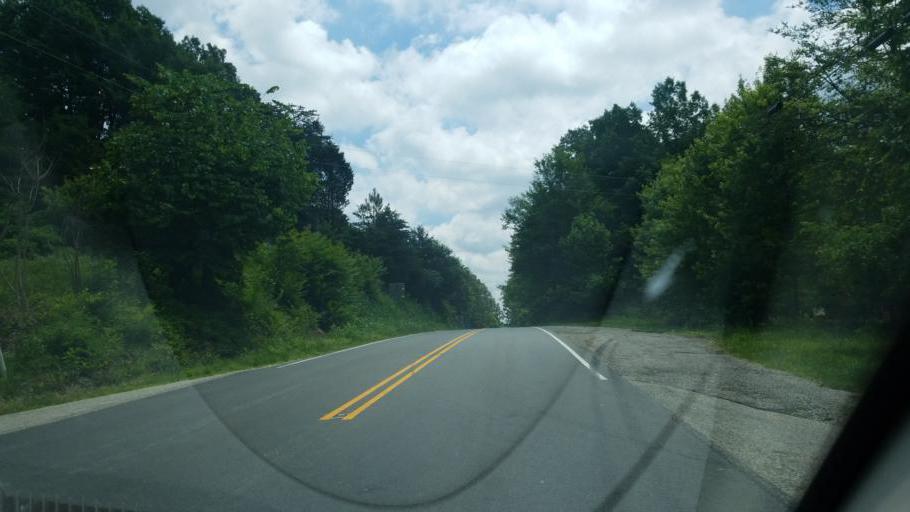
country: US
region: Virginia
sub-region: Nelson County
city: Lovingston
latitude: 37.5716
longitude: -78.8564
